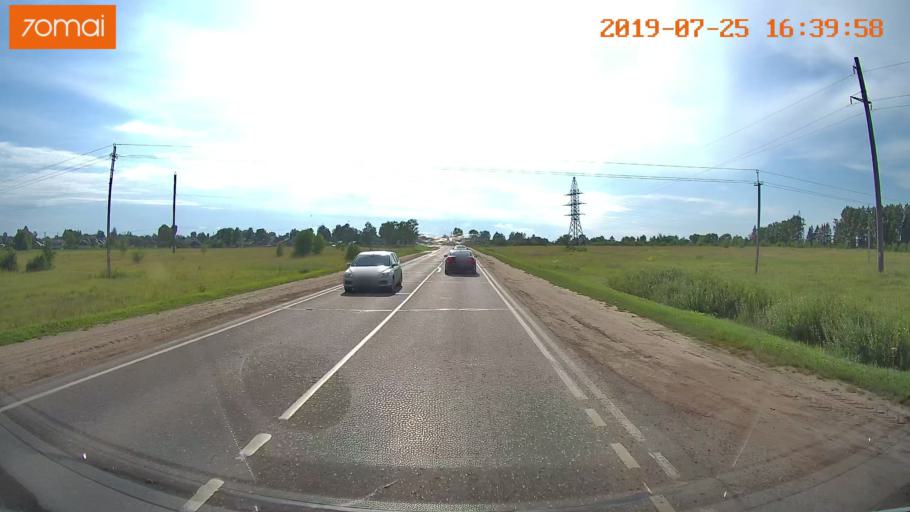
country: RU
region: Ivanovo
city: Privolzhsk
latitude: 57.3866
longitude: 41.3151
